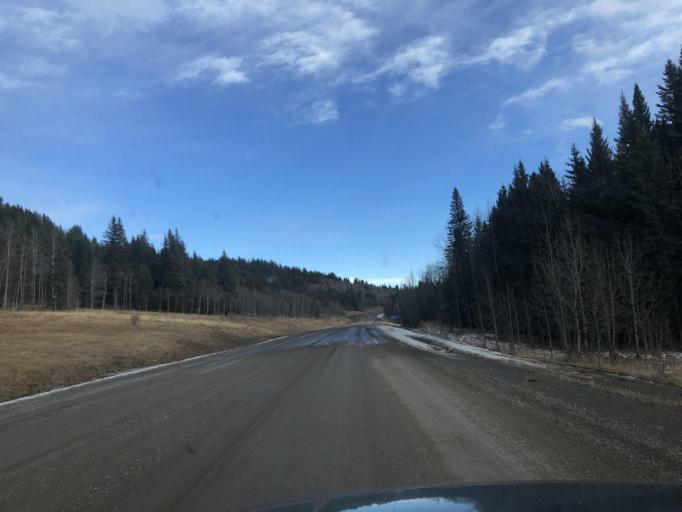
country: CA
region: Alberta
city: Cochrane
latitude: 51.0435
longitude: -114.7611
